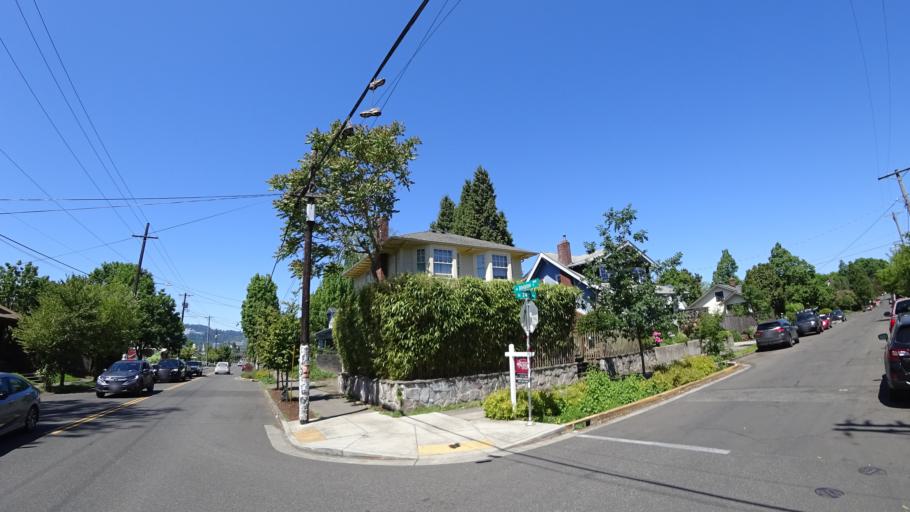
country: US
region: Oregon
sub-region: Multnomah County
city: Portland
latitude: 45.5048
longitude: -122.6412
